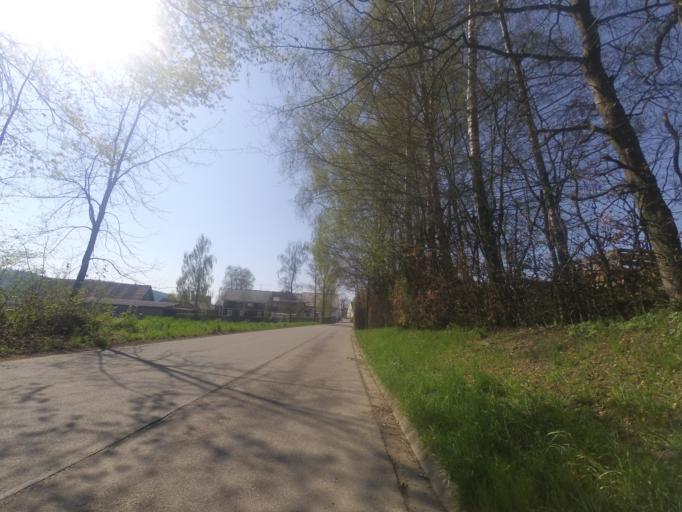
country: DE
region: Bavaria
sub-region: Swabia
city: Pfaffenhofen an der Roth
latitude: 48.3856
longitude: 10.1757
